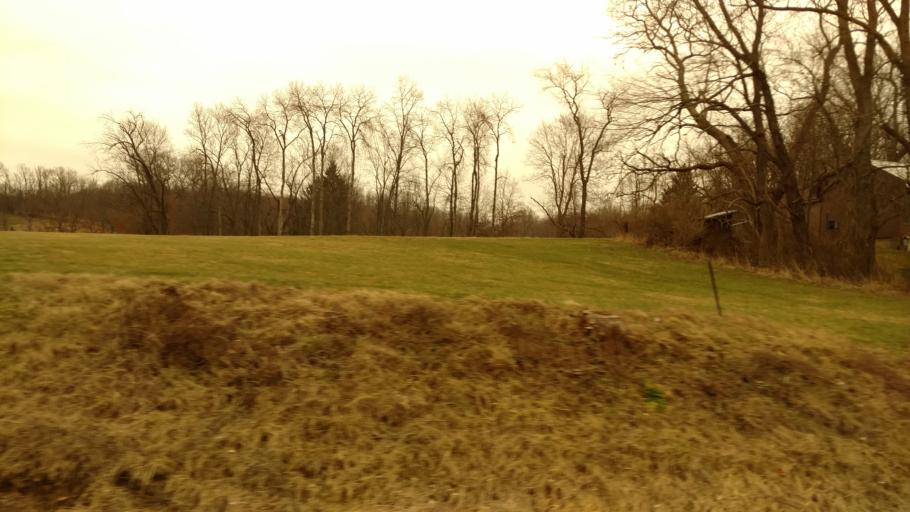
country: US
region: Ohio
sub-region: Knox County
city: Mount Vernon
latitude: 40.4090
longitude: -82.4563
